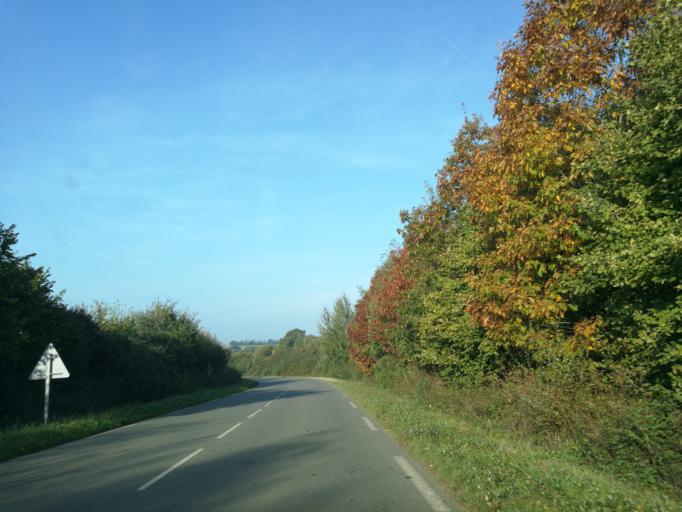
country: FR
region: Brittany
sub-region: Departement d'Ille-et-Vilaine
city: Breteil
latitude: 48.1696
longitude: -1.8996
